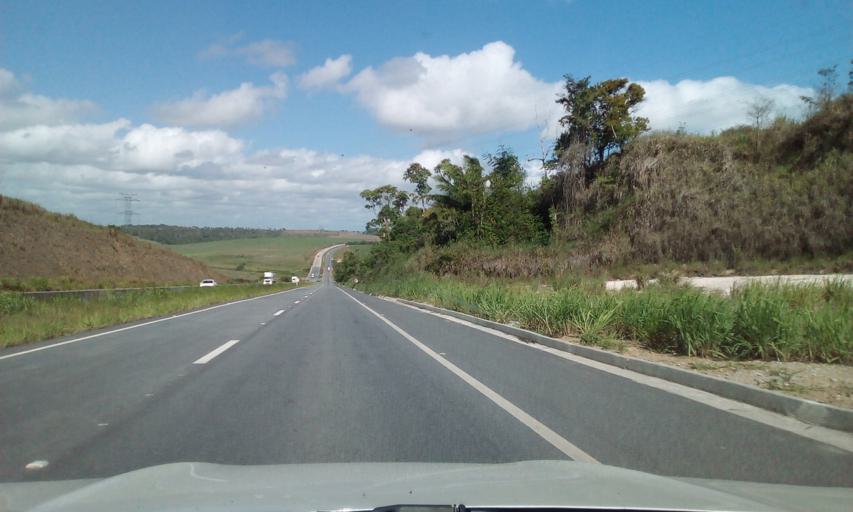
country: BR
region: Alagoas
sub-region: Rio Largo
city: Rio Largo
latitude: -9.4509
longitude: -35.8688
